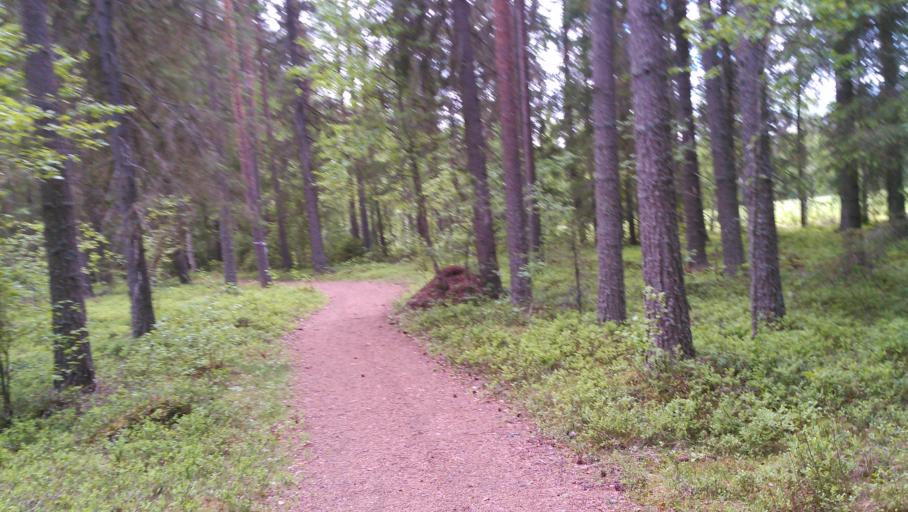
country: SE
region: Vaesterbotten
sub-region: Vannas Kommun
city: Vannasby
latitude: 64.0183
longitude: 19.9025
